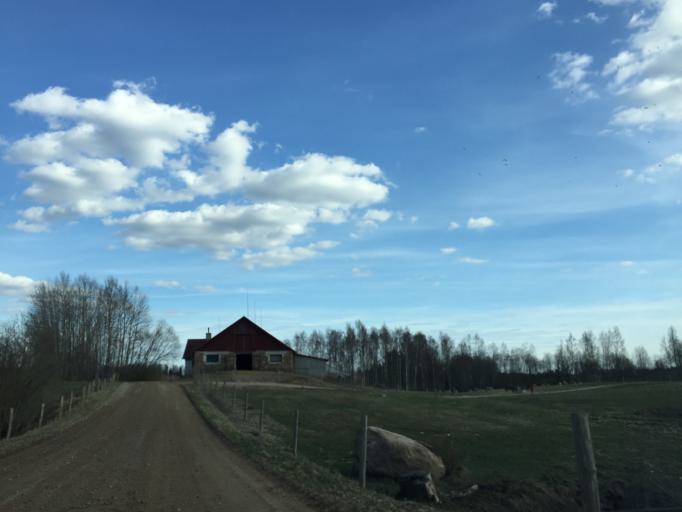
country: EE
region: Tartu
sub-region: Noo vald
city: Noo
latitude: 58.1347
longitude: 26.5933
